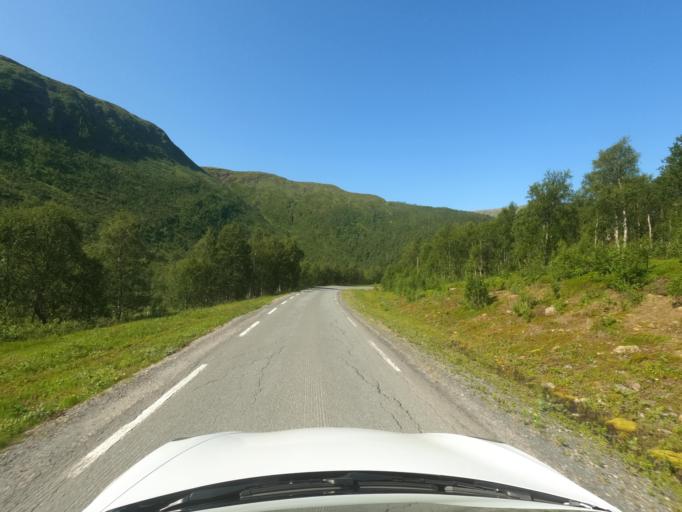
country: NO
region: Troms
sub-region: Skanland
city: Evenskjer
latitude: 68.3292
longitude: 16.5470
